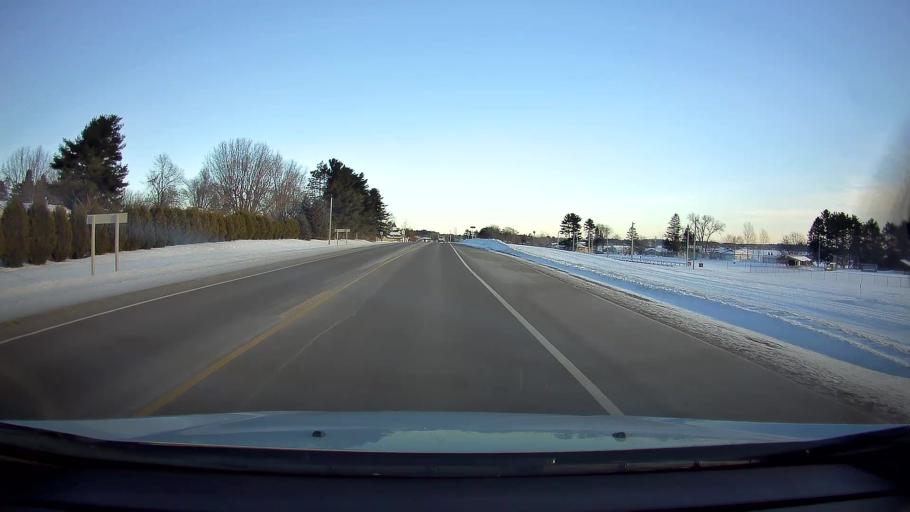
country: US
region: Wisconsin
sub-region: Washburn County
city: Shell Lake
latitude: 45.7366
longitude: -91.9275
